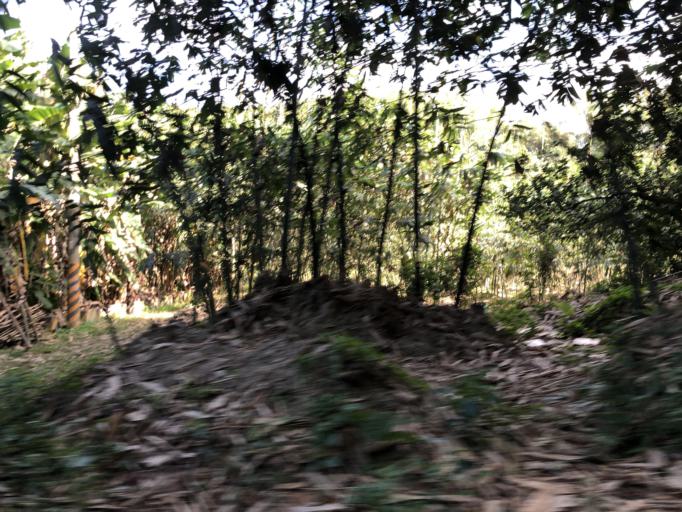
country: TW
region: Taiwan
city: Yujing
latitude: 23.0112
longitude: 120.3982
